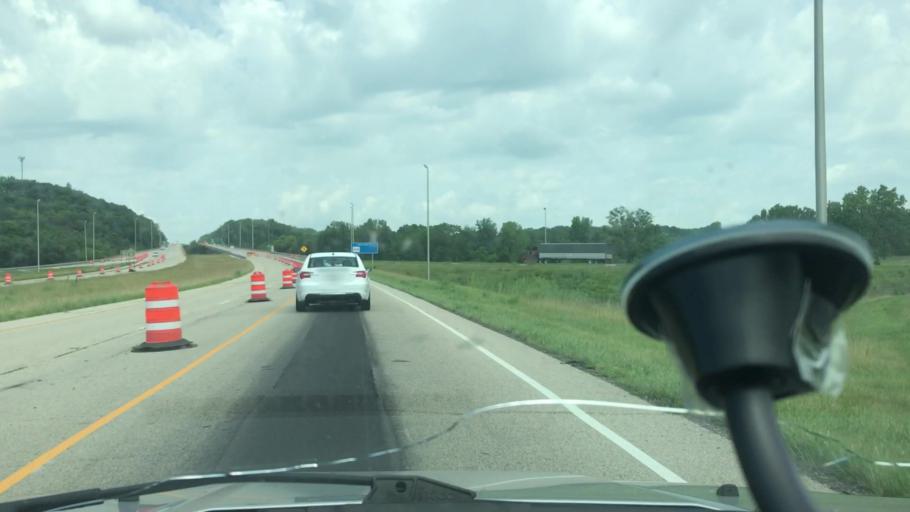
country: US
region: Illinois
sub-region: Peoria County
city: Bartonville
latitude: 40.6584
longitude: -89.6451
